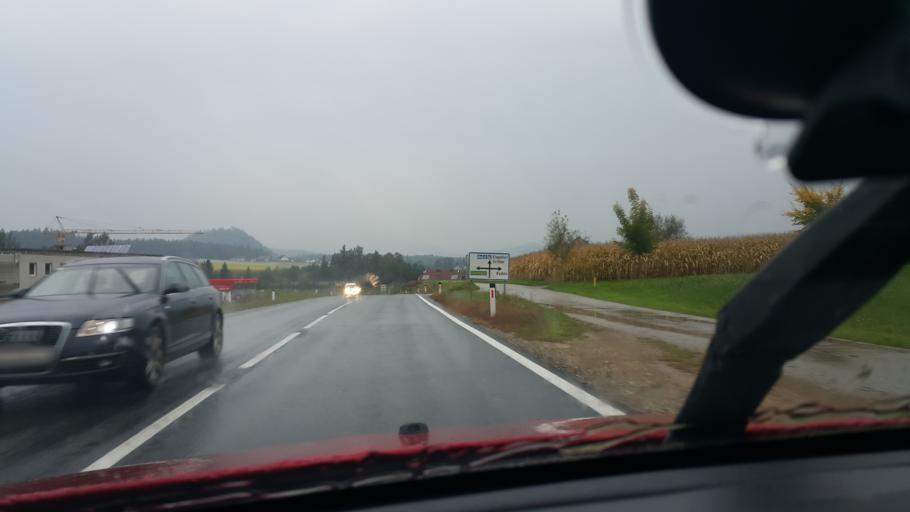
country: AT
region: Carinthia
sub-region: Politischer Bezirk Volkermarkt
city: Ruden
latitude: 46.6486
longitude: 14.7711
